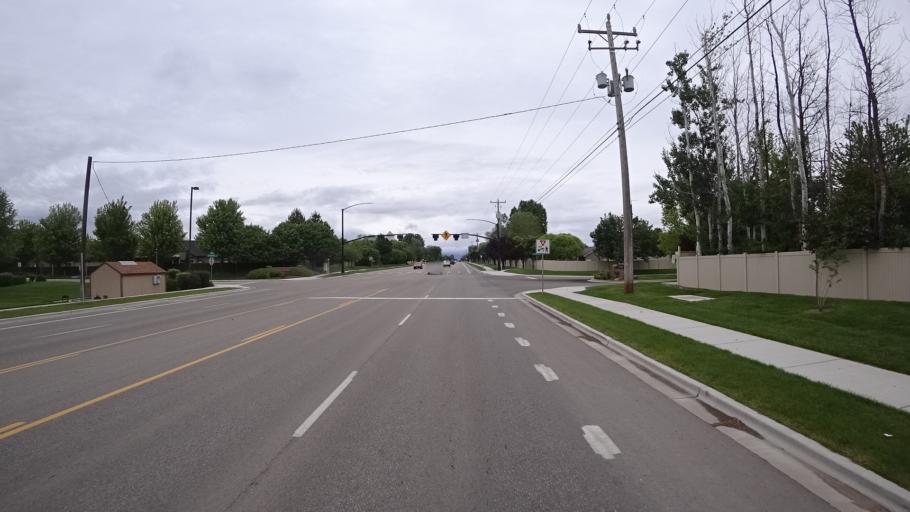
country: US
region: Idaho
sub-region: Ada County
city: Meridian
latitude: 43.6337
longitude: -116.3877
